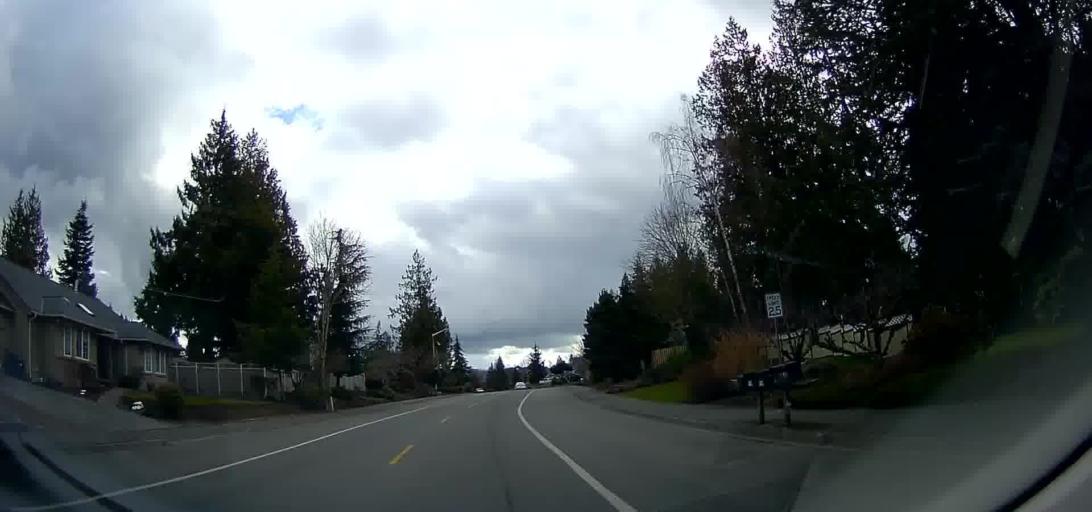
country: US
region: Washington
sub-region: Skagit County
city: Mount Vernon
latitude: 48.4196
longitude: -122.2873
